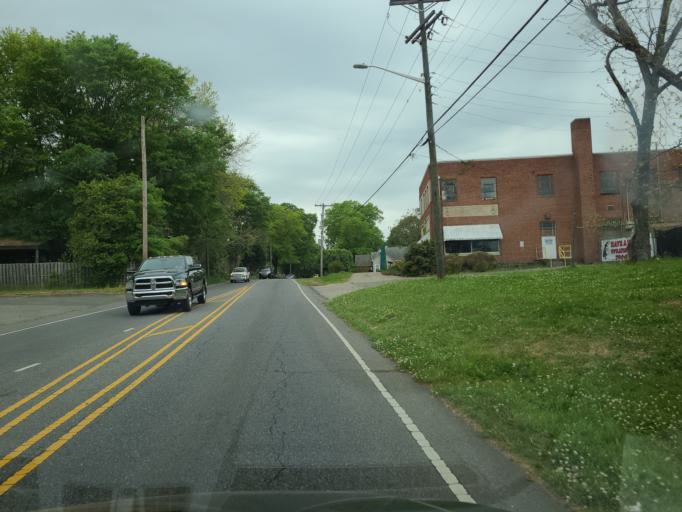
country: US
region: North Carolina
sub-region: Cleveland County
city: Shelby
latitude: 35.2960
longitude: -81.5211
